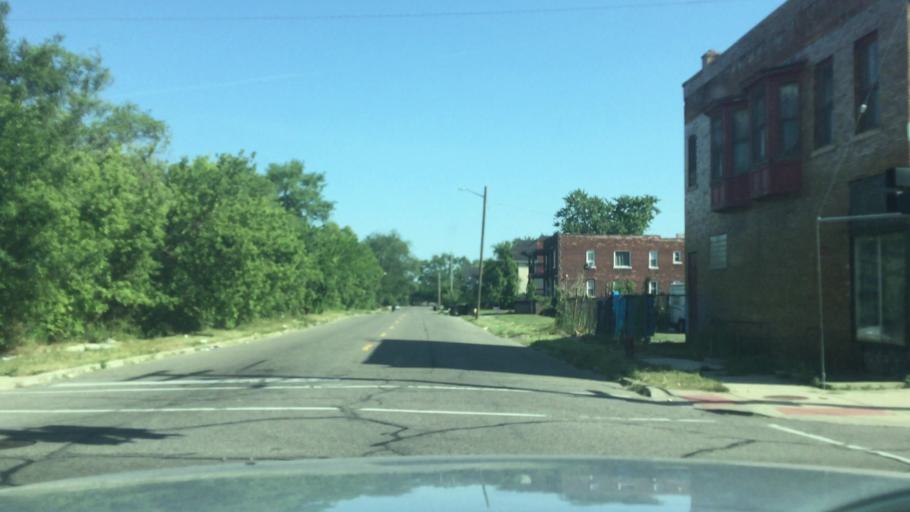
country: US
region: Michigan
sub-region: Wayne County
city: Grosse Pointe Park
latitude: 42.3632
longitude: -82.9878
